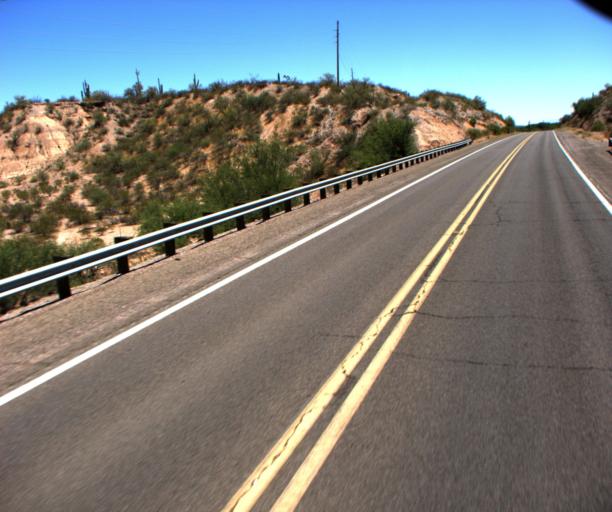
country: US
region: Arizona
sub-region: Pinal County
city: Kearny
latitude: 32.9364
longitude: -110.7364
